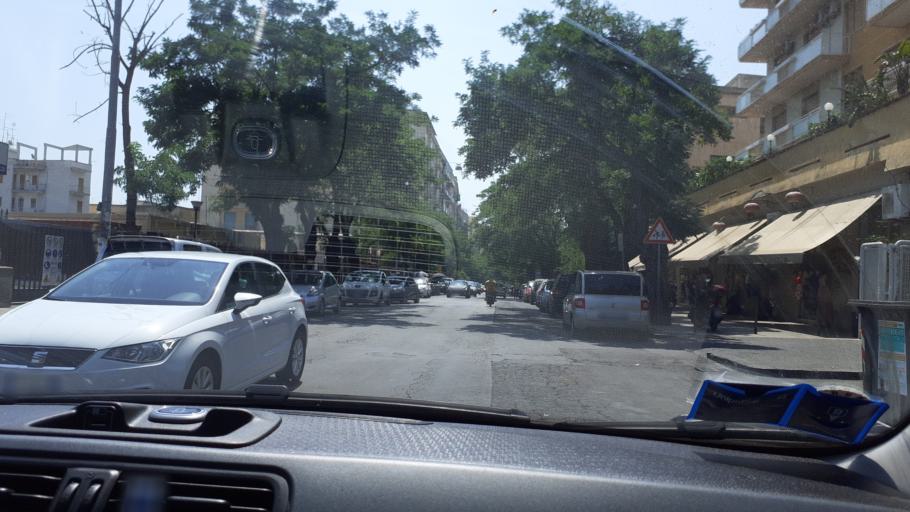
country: IT
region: Sicily
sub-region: Catania
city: Catania
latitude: 37.5110
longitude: 15.0750
